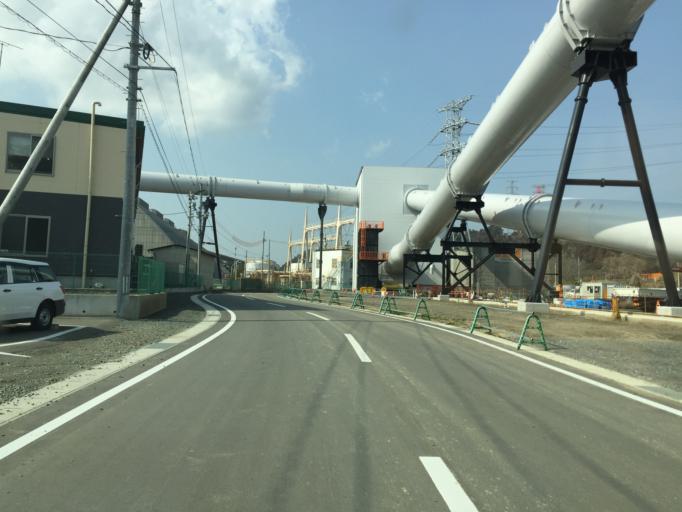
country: JP
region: Ibaraki
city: Kitaibaraki
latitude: 36.9157
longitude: 140.8156
